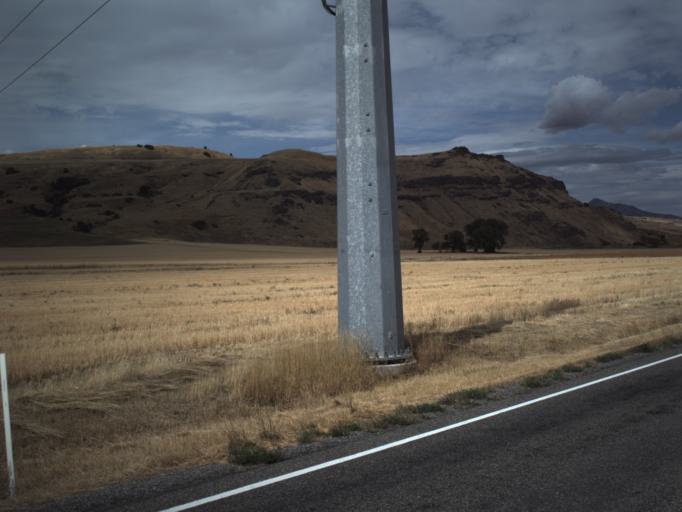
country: US
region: Utah
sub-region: Cache County
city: Benson
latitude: 41.7843
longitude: -111.9866
